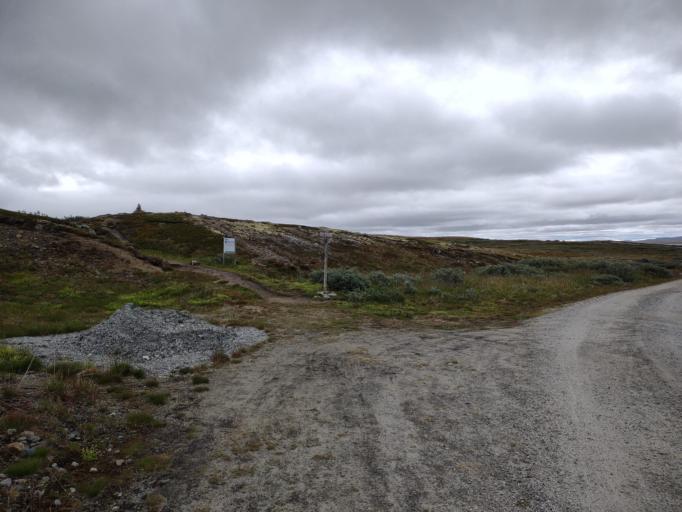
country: NO
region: Hordaland
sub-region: Eidfjord
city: Eidfjord
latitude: 60.2849
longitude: 7.5753
